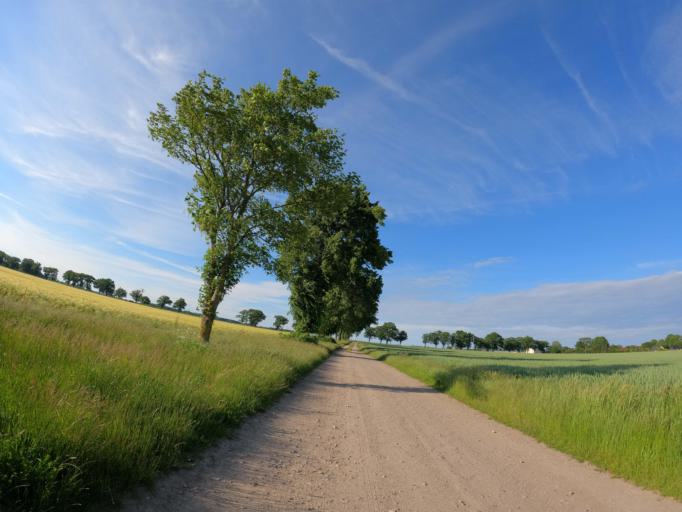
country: DE
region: Mecklenburg-Vorpommern
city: Preetz
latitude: 54.3462
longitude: 13.0007
